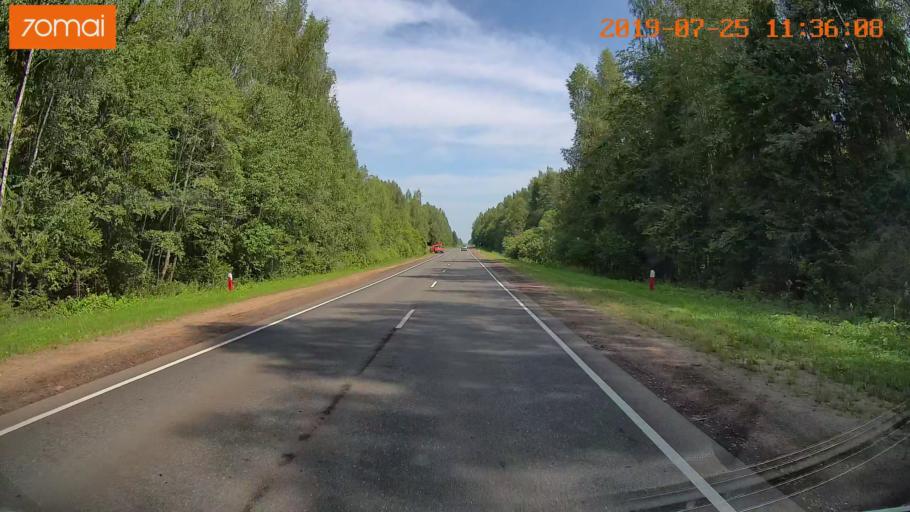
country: RU
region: Ivanovo
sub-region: Privolzhskiy Rayon
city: Ples
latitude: 57.4197
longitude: 41.4428
